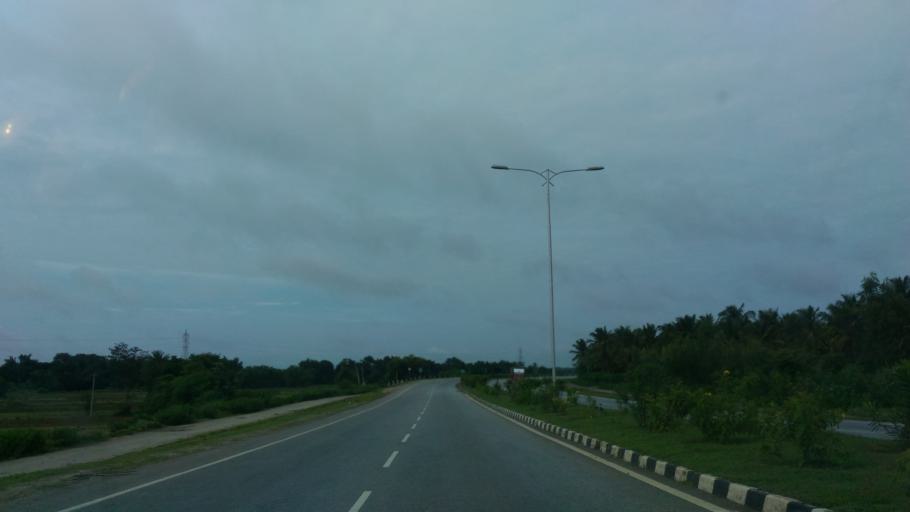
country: IN
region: Karnataka
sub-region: Tumkur
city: Kunigal
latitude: 13.0264
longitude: 77.0753
